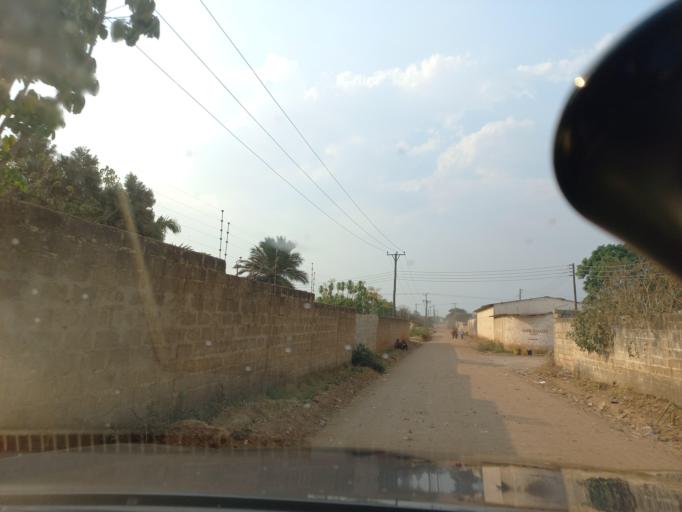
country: ZM
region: Lusaka
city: Lusaka
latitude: -15.4769
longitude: 28.2043
